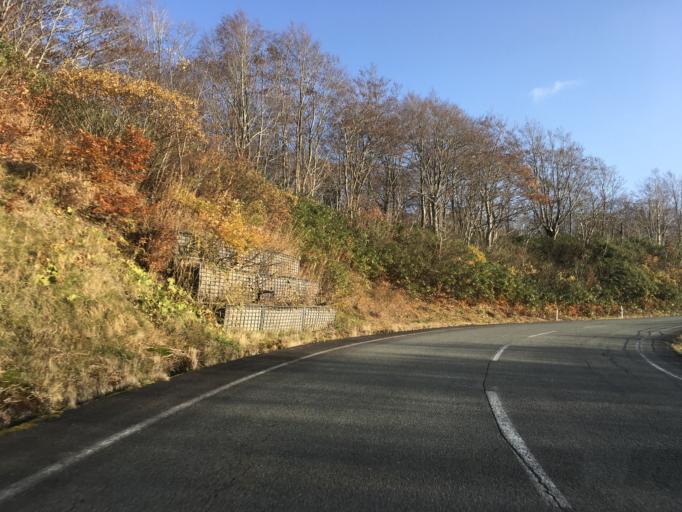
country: JP
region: Akita
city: Yuzawa
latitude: 38.9880
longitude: 140.7641
